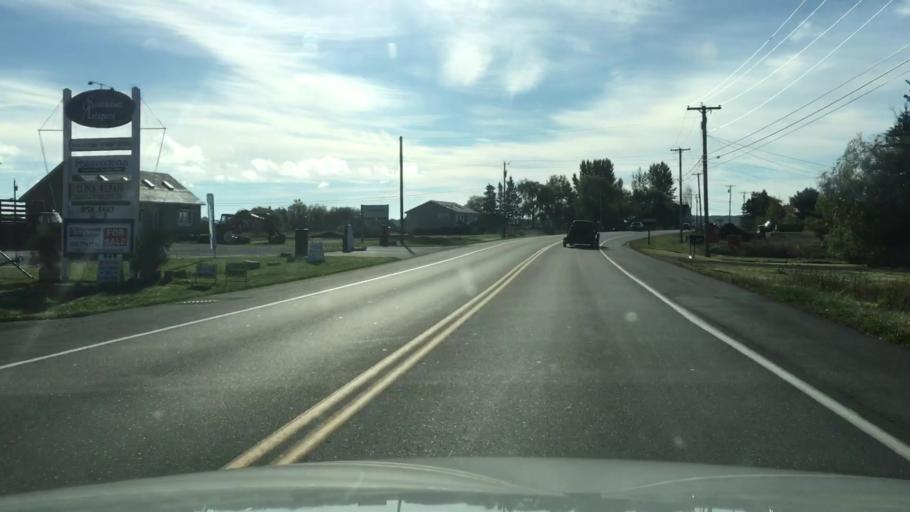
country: US
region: Maine
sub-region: Knox County
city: Warren
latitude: 44.0837
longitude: -69.2276
